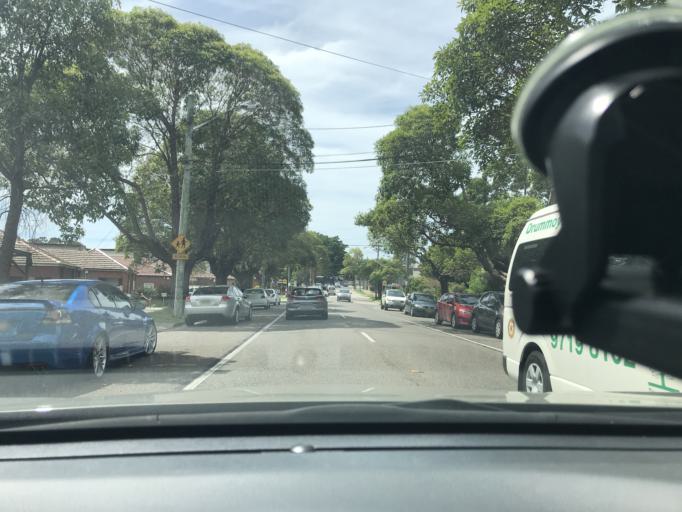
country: AU
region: New South Wales
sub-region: Canada Bay
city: Wareemba
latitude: -33.8642
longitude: 151.1281
